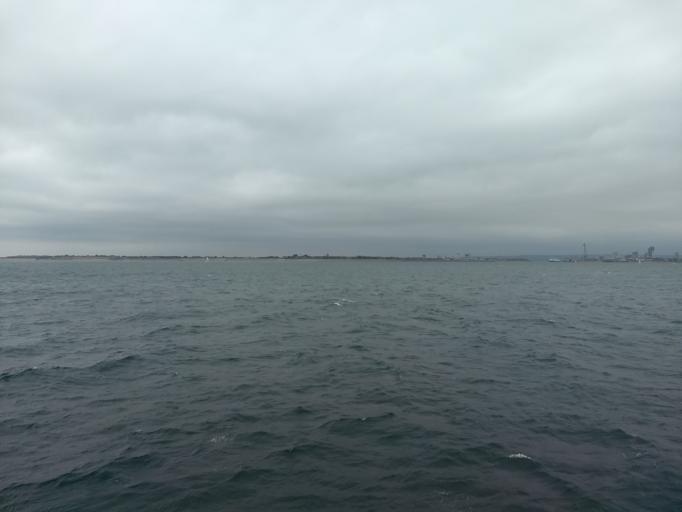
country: GB
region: England
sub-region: Portsmouth
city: Southsea
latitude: 50.7632
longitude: -1.1072
